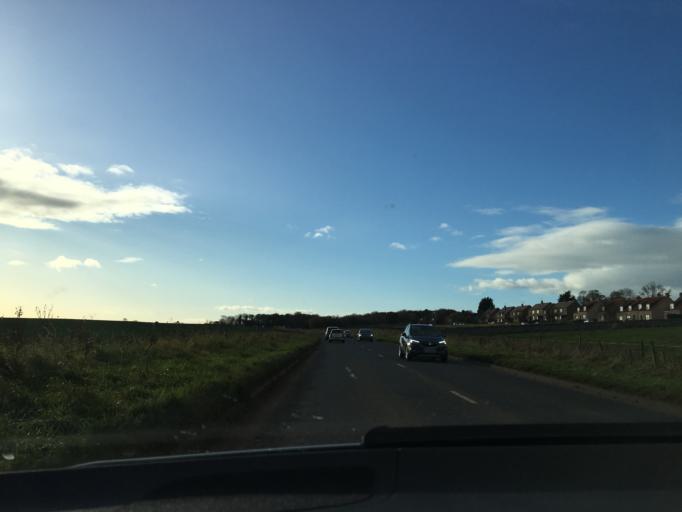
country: GB
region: Scotland
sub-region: East Lothian
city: Gullane
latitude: 56.0447
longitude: -2.7765
